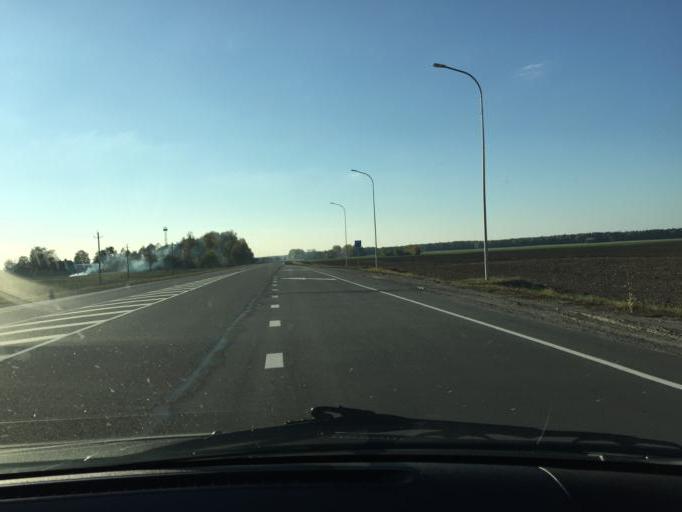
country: BY
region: Brest
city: Horad Luninyets
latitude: 52.3169
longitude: 26.6263
